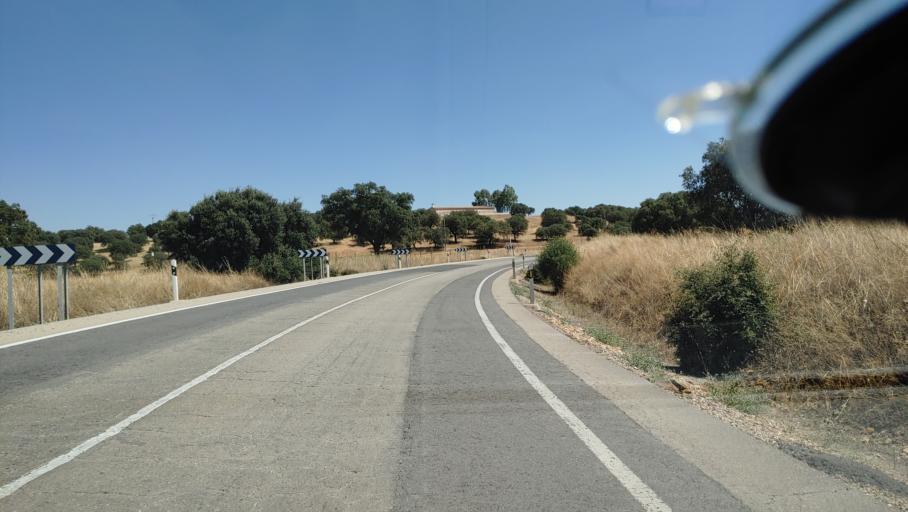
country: ES
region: Castille-La Mancha
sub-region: Provincia de Ciudad Real
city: Saceruela
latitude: 39.0189
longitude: -4.4889
